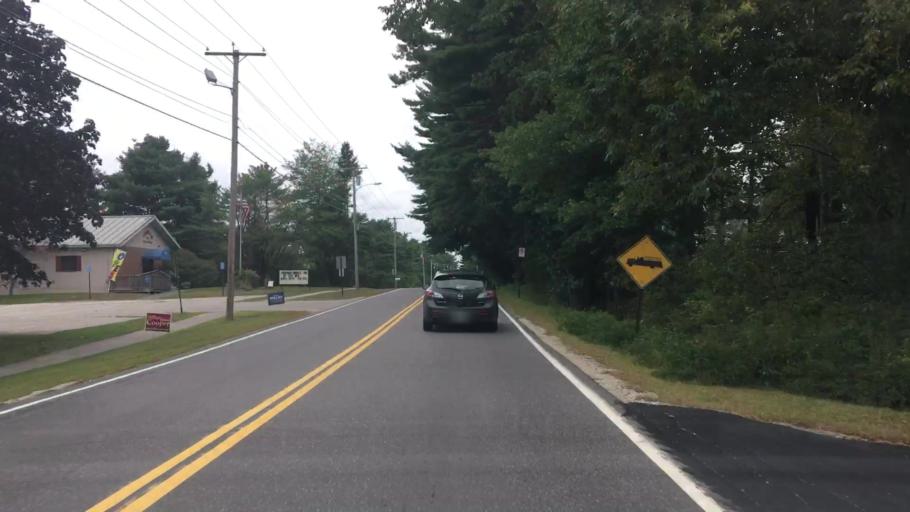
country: US
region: Maine
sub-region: Cumberland County
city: Yarmouth
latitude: 43.8108
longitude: -70.1777
